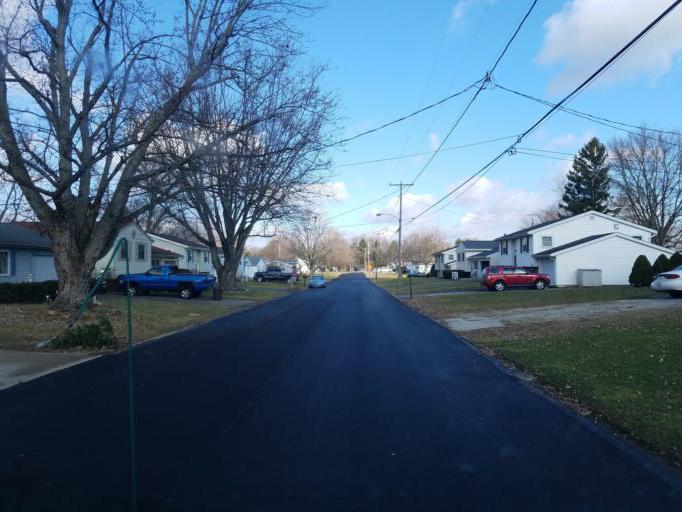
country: US
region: Ohio
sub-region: Marion County
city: Marion
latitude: 40.5683
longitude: -83.1593
